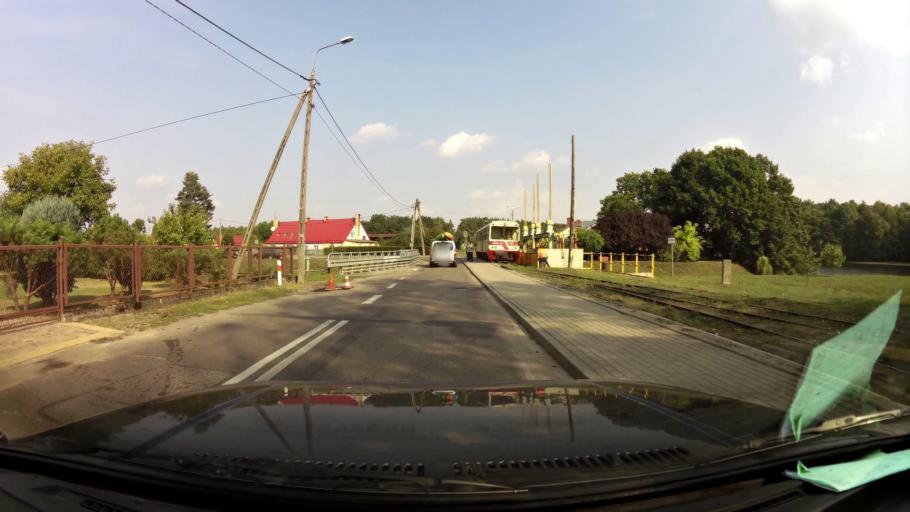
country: PL
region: West Pomeranian Voivodeship
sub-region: Powiat bialogardzki
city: Tychowo
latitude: 54.0684
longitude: 16.2984
